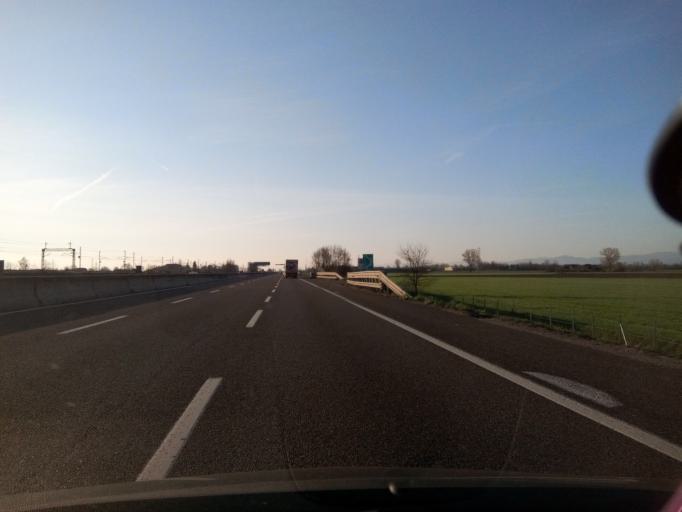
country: IT
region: Emilia-Romagna
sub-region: Provincia di Piacenza
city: Pontenure
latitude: 45.0275
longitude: 9.7718
